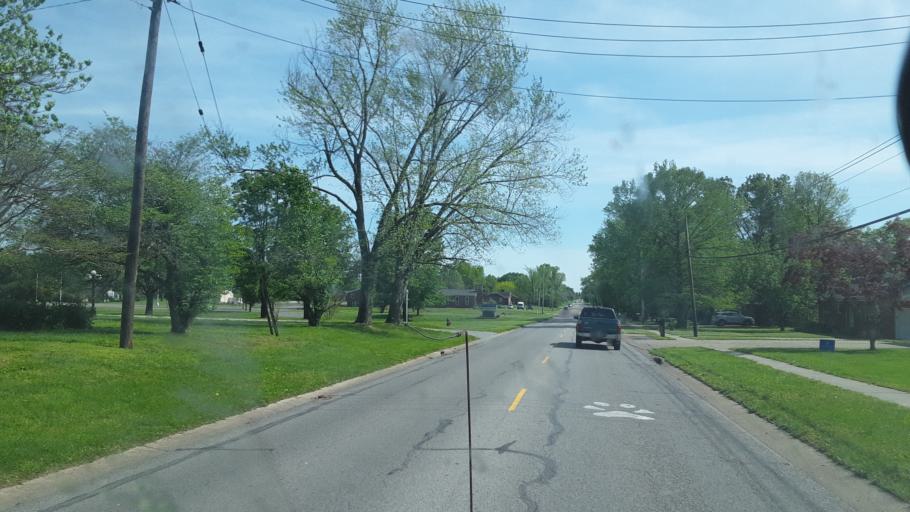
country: US
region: Illinois
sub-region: Jackson County
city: Carbondale
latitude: 37.7212
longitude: -89.1852
